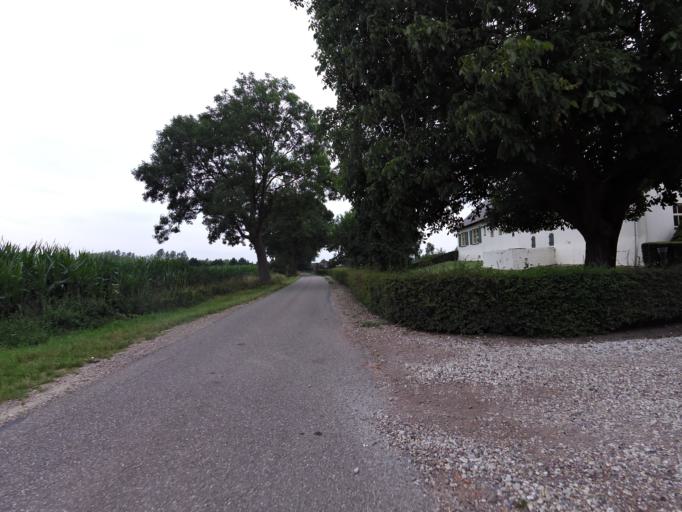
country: NL
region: Gelderland
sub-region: Gemeente Groesbeek
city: Berg en Dal
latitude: 51.8456
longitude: 5.9398
